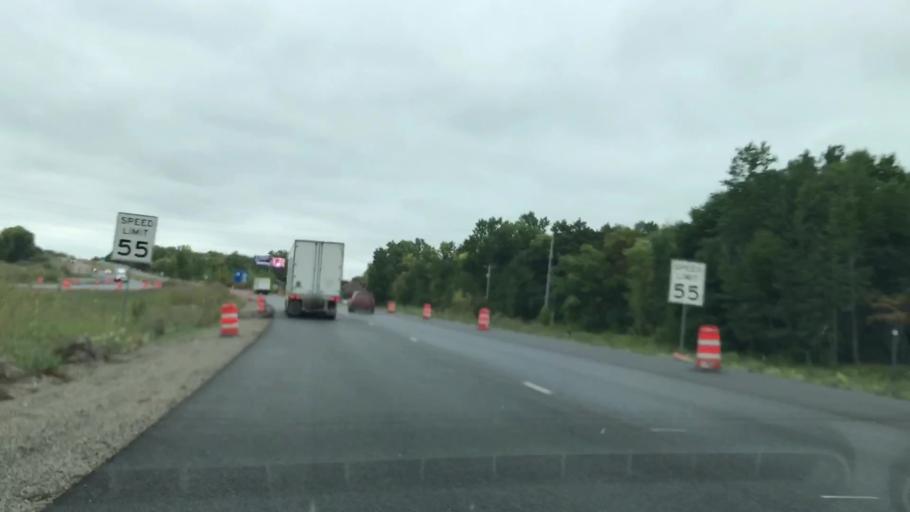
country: US
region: Wisconsin
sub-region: Brown County
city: Suamico
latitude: 44.6473
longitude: -88.0500
